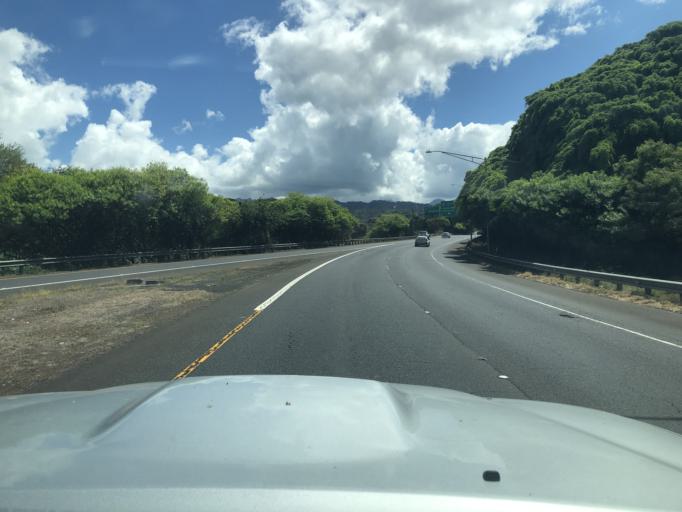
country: US
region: Hawaii
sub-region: Honolulu County
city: Halawa
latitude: 21.3703
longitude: -157.9232
